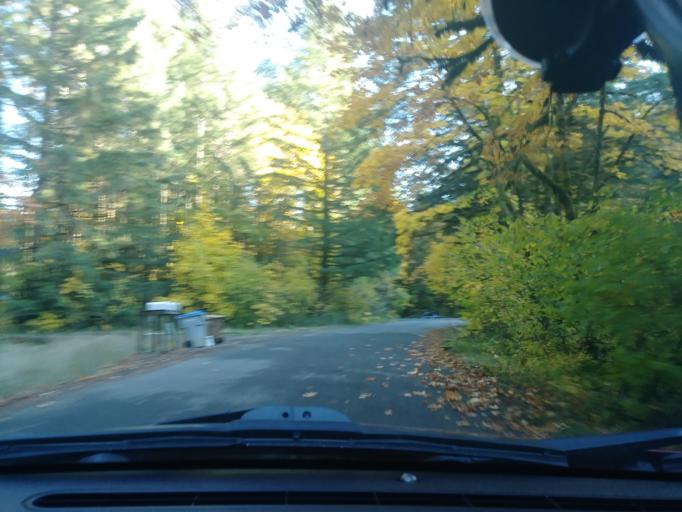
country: US
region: Oregon
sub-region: Washington County
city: Banks
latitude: 45.6549
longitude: -123.3015
